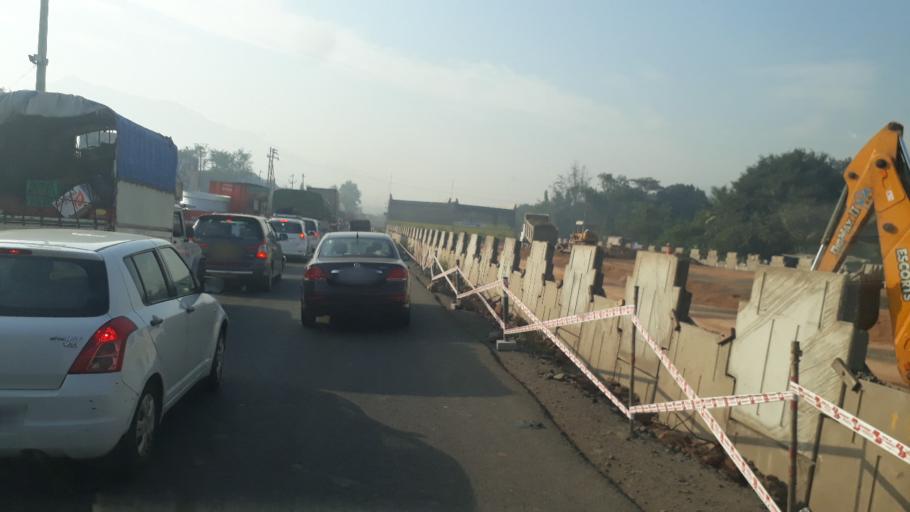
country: IN
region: Maharashtra
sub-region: Raigarh
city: Kalundri
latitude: 18.9274
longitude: 73.1267
